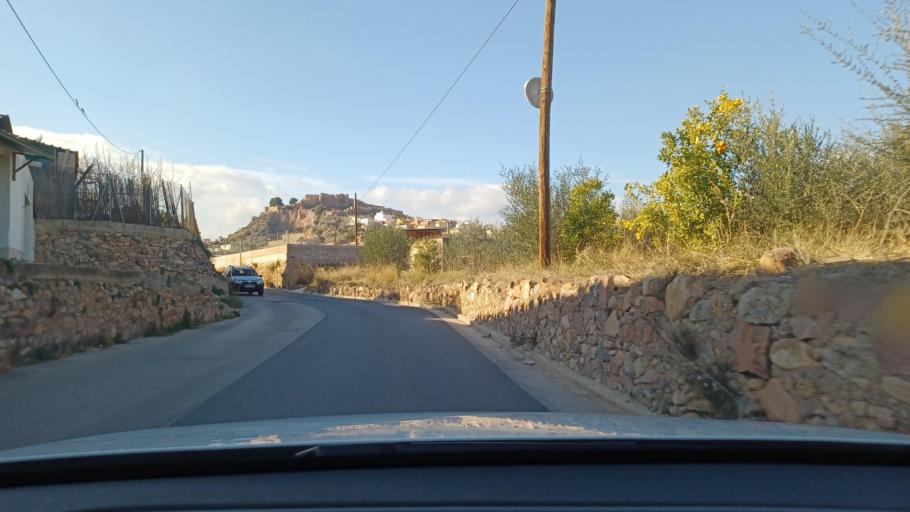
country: ES
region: Valencia
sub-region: Provincia de Castello
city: Onda
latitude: 39.9597
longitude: -0.2522
